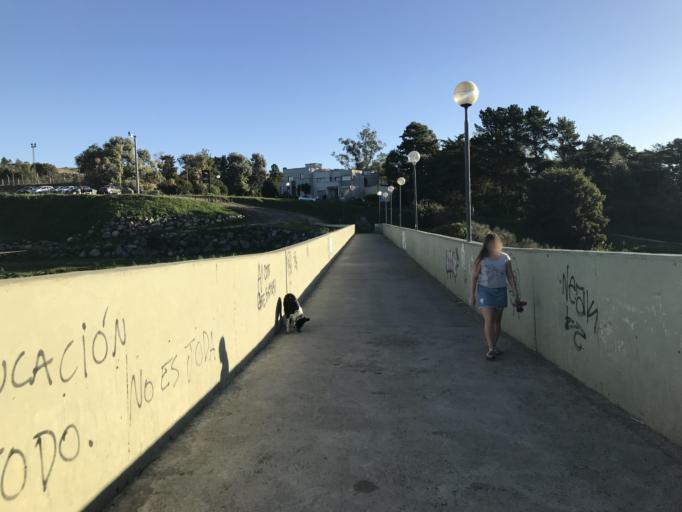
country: AR
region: Buenos Aires
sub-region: Partido de Tandil
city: Tandil
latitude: -37.3375
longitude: -59.1144
